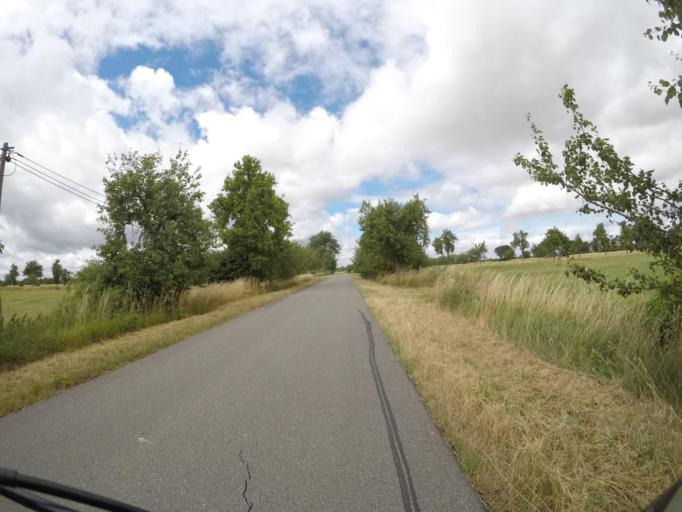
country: DE
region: Lower Saxony
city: Dannenberg
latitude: 53.1500
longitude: 11.1019
